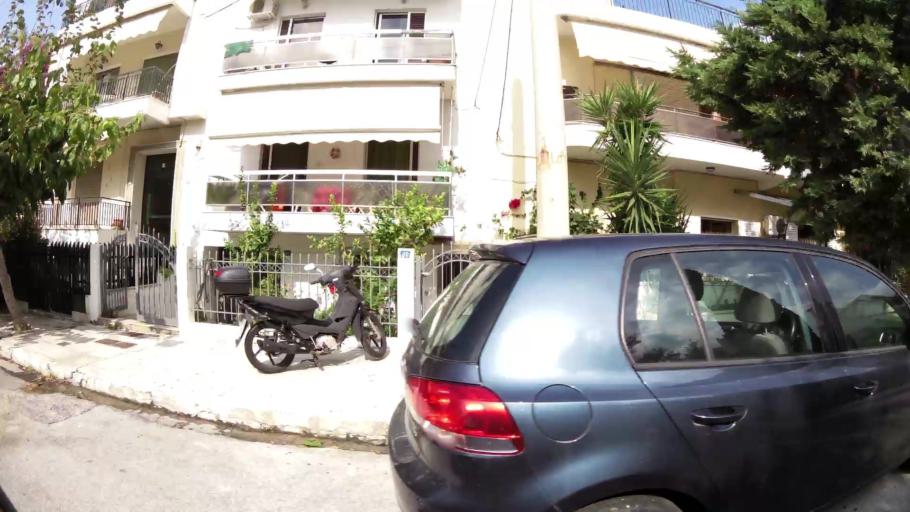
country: GR
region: Attica
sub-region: Nomarchia Athinas
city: Ilioupoli
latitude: 37.9409
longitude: 23.7595
